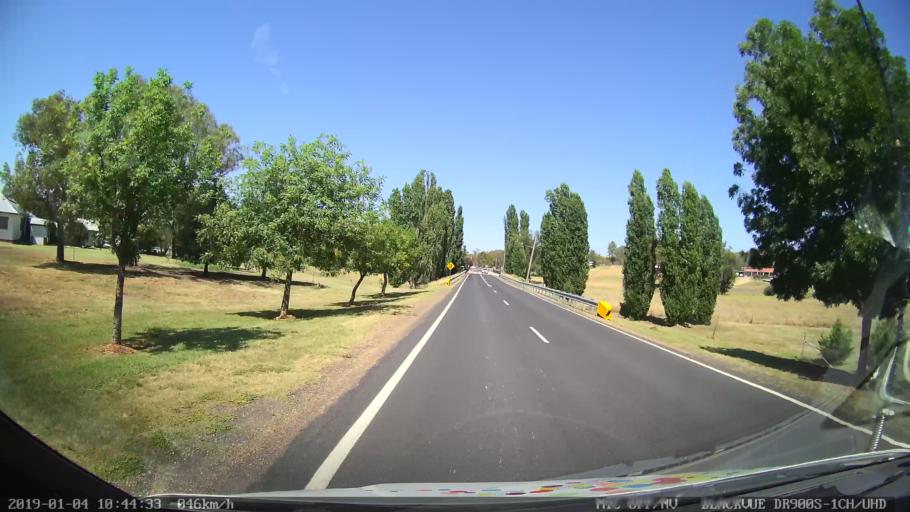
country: AU
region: New South Wales
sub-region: Cabonne
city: Molong
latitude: -33.2879
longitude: 148.7362
